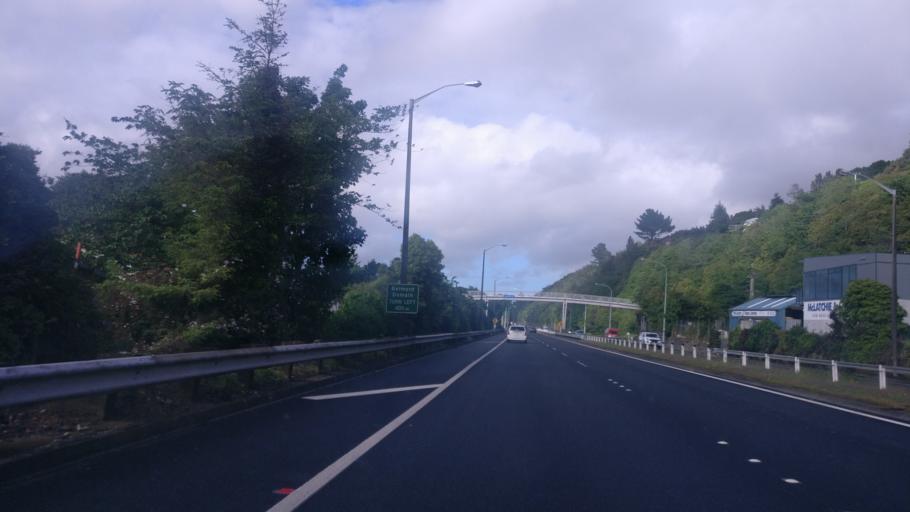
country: NZ
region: Wellington
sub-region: Lower Hutt City
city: Lower Hutt
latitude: -41.1853
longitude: 174.9379
